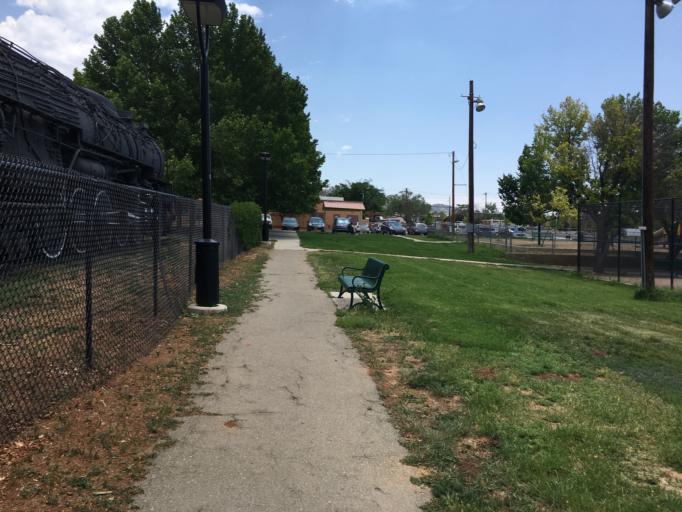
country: US
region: New Mexico
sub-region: Santa Fe County
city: Santa Fe
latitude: 35.6712
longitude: -105.9528
